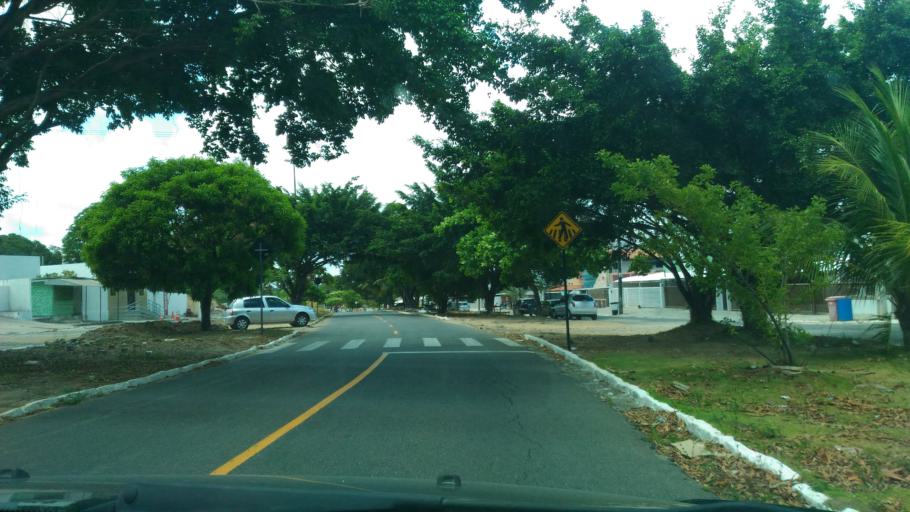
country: BR
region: Paraiba
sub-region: Joao Pessoa
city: Joao Pessoa
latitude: -7.1487
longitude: -34.8337
